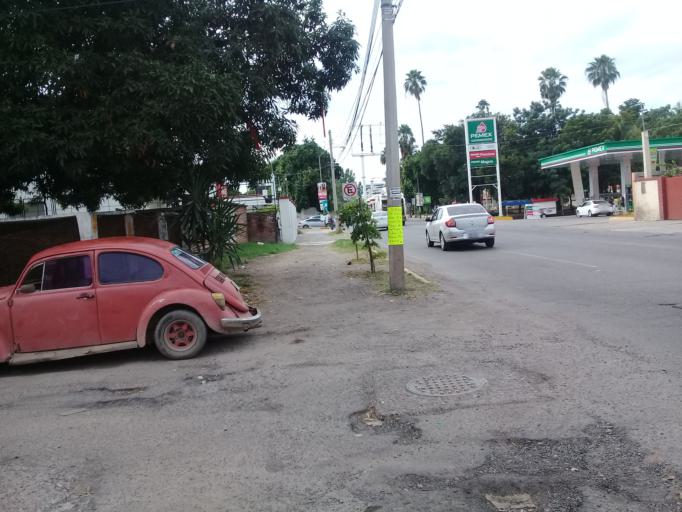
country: MX
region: Sinaloa
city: Culiacan
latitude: 24.8184
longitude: -107.3962
